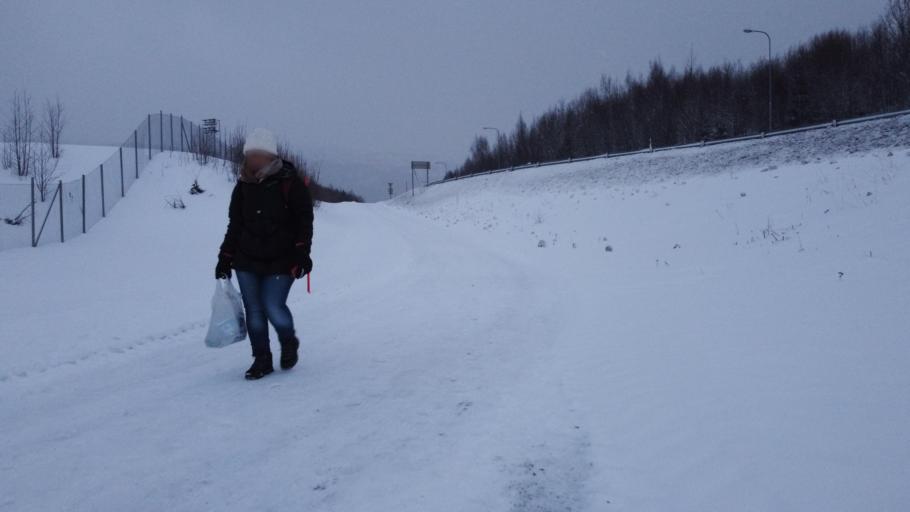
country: NO
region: Nordland
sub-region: Rana
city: Mo i Rana
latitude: 66.3241
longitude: 14.1586
